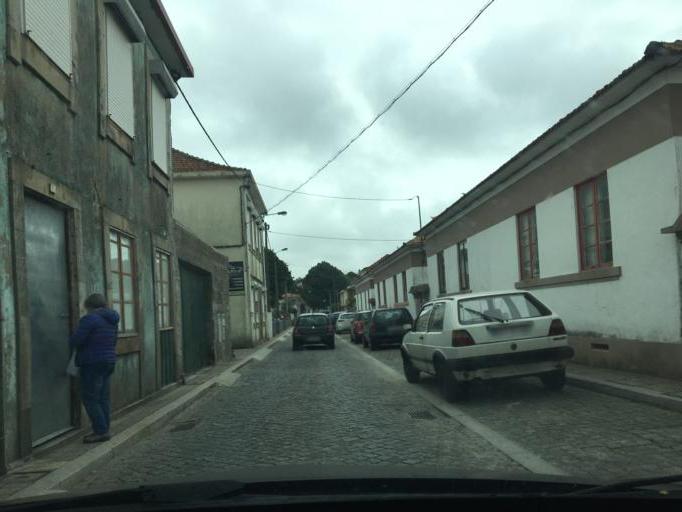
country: PT
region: Porto
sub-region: Matosinhos
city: Santa Cruz do Bispo
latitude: 41.2196
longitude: -8.6761
